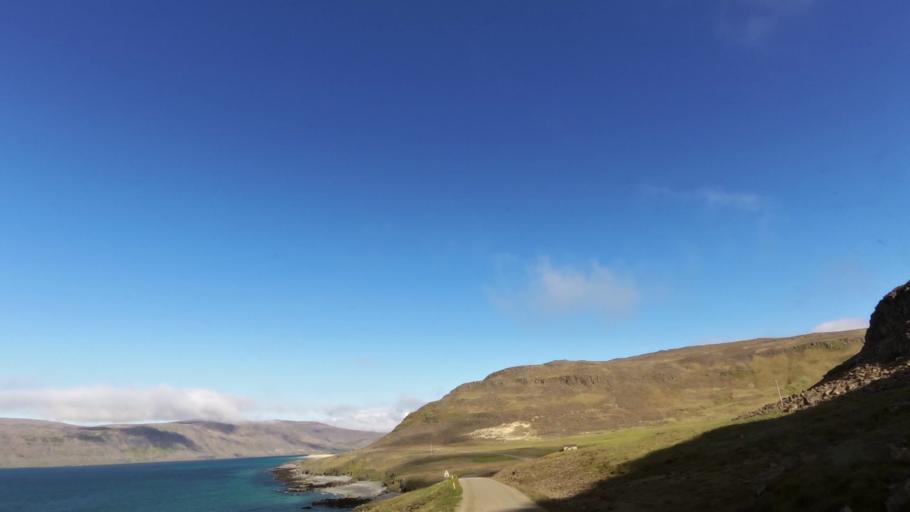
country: IS
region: West
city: Olafsvik
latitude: 65.5606
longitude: -24.0191
